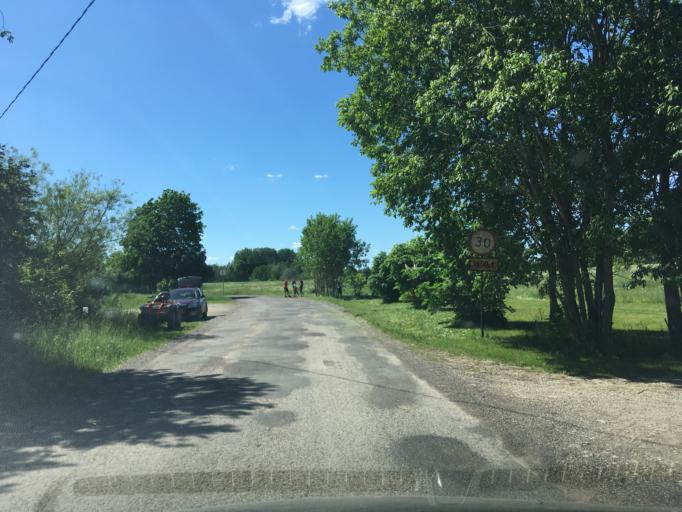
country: EE
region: Harju
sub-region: Rae vald
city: Vaida
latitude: 59.1703
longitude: 25.1243
